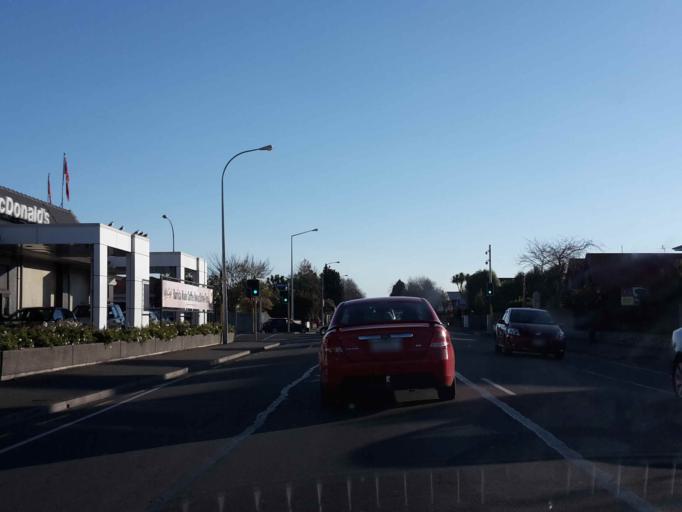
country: NZ
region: Canterbury
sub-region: Christchurch City
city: Christchurch
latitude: -43.5300
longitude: 172.5963
